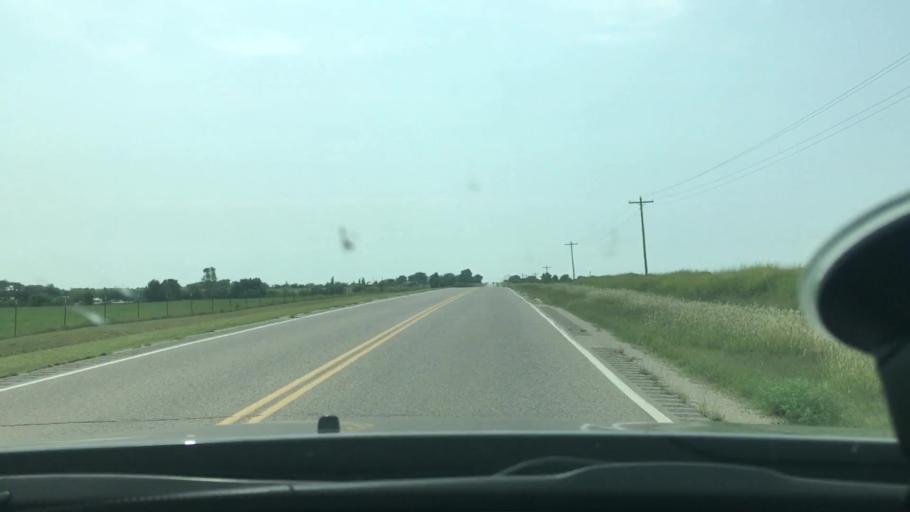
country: US
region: Oklahoma
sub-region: Marshall County
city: Madill
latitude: 34.0413
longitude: -96.7611
